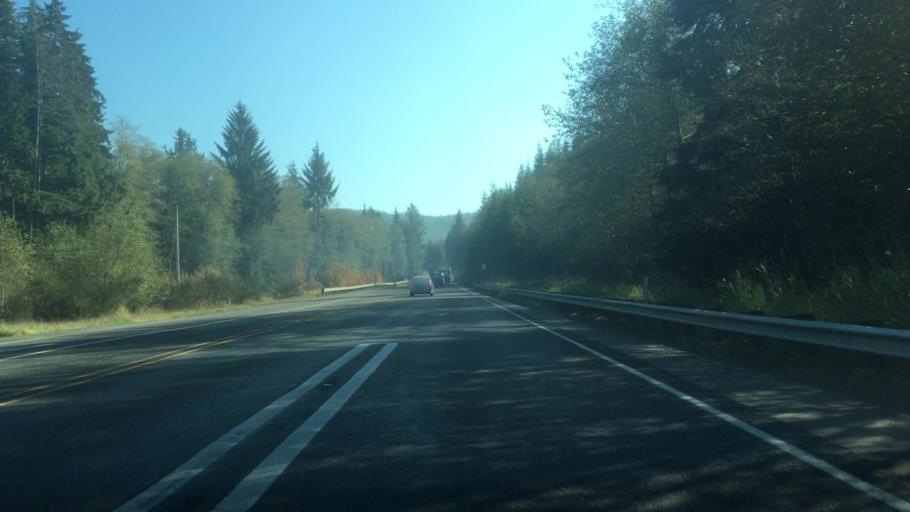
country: US
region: Washington
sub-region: Grays Harbor County
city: Central Park
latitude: 46.9178
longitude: -123.7192
